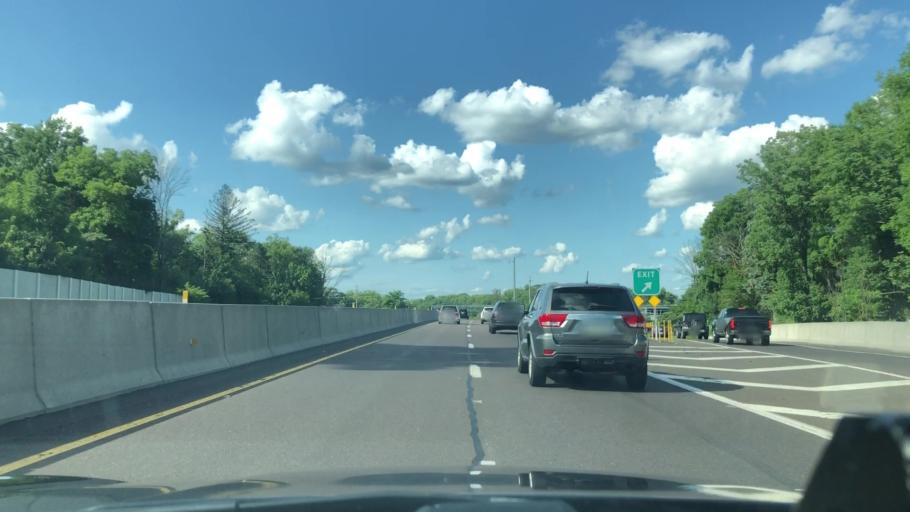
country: US
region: Pennsylvania
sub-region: Montgomery County
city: Spring House
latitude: 40.1779
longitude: -75.2130
